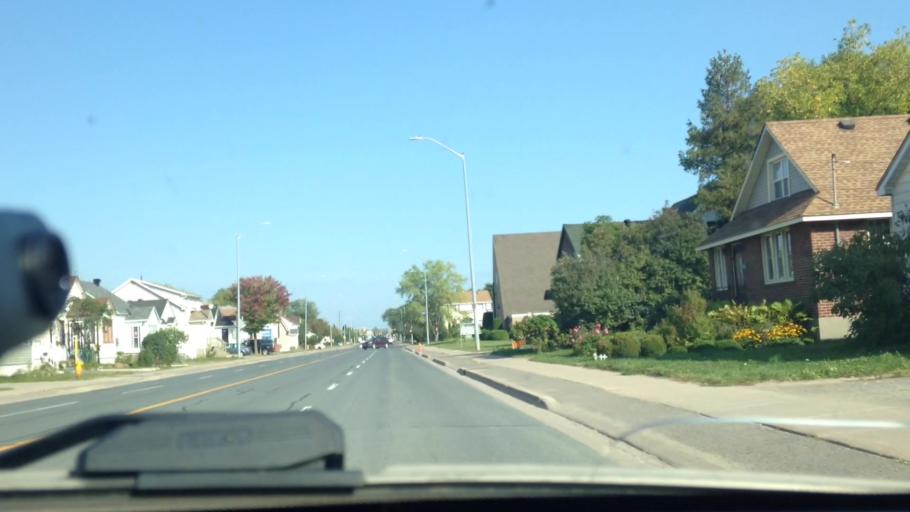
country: CA
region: Ontario
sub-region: Algoma
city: Sault Ste. Marie
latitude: 46.5092
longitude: -84.3132
